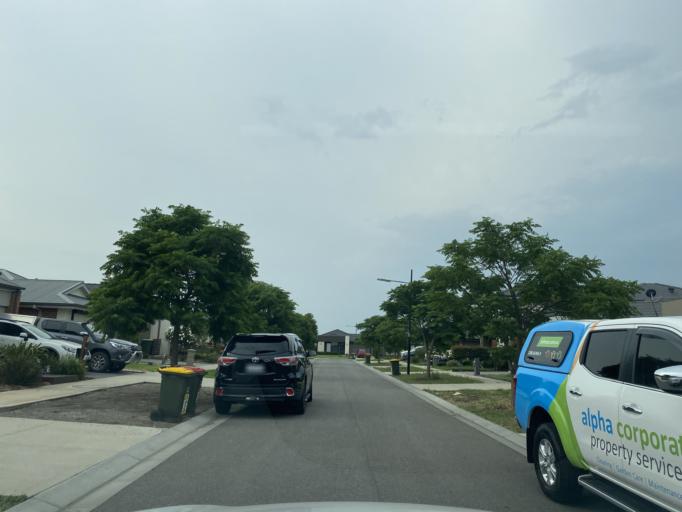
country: AU
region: Victoria
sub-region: Hume
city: Greenvale
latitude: -37.6234
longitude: 144.8754
